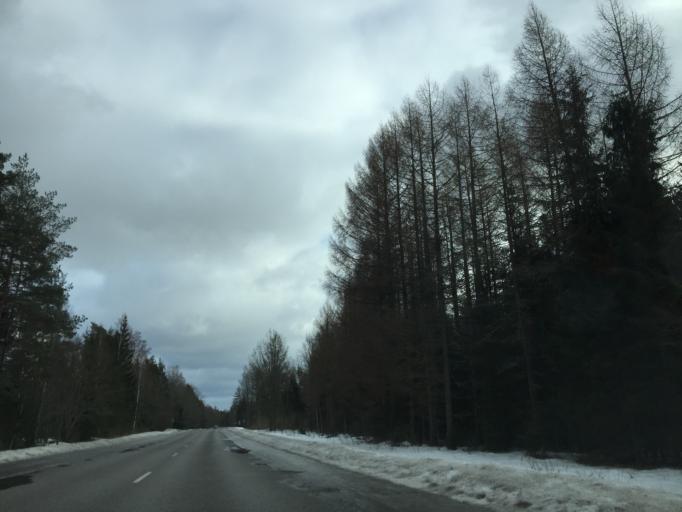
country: LV
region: Aloja
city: Staicele
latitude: 57.8194
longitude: 24.7800
